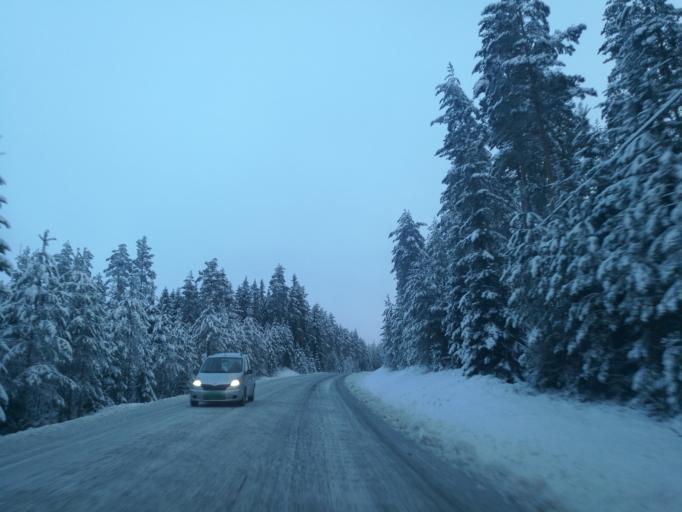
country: NO
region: Hedmark
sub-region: Grue
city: Kirkenaer
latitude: 60.3255
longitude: 12.2830
